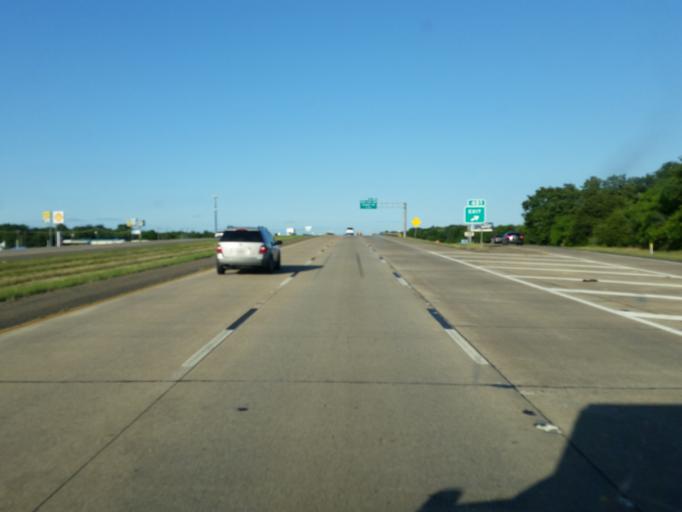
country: US
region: Texas
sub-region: Dallas County
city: Balch Springs
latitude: 32.7021
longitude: -96.6088
